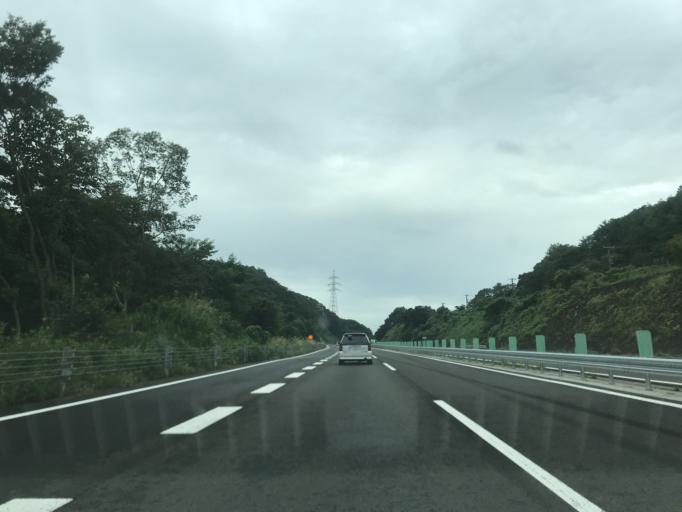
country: JP
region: Miyagi
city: Sendai
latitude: 38.2731
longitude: 140.8099
